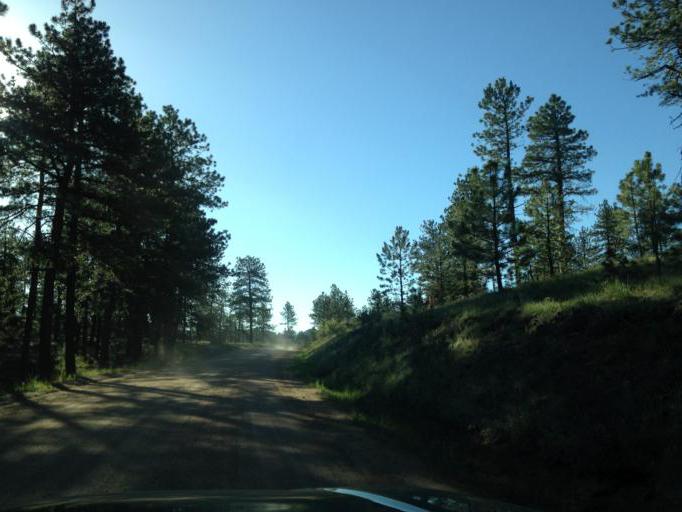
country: US
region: Colorado
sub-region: Jefferson County
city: Evergreen
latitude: 39.4032
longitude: -105.4954
